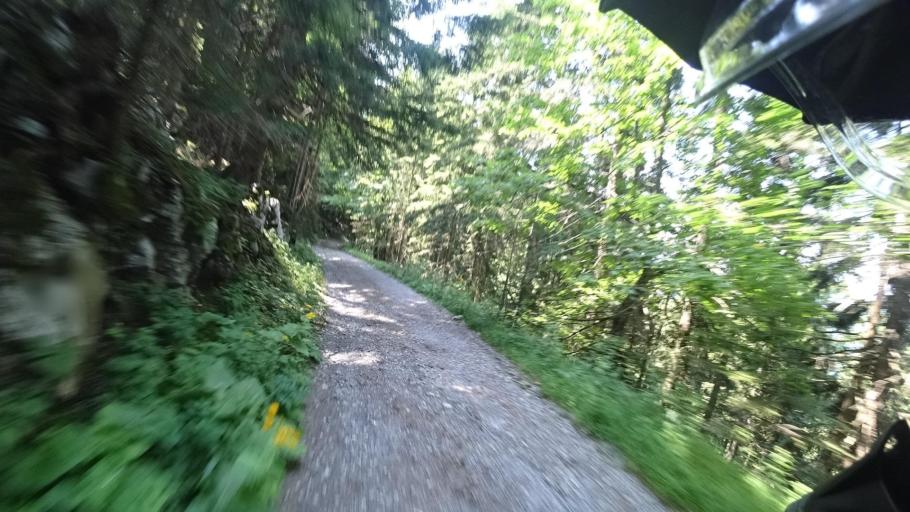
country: HR
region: Primorsko-Goranska
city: Vrbovsko
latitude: 45.3348
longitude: 15.0214
